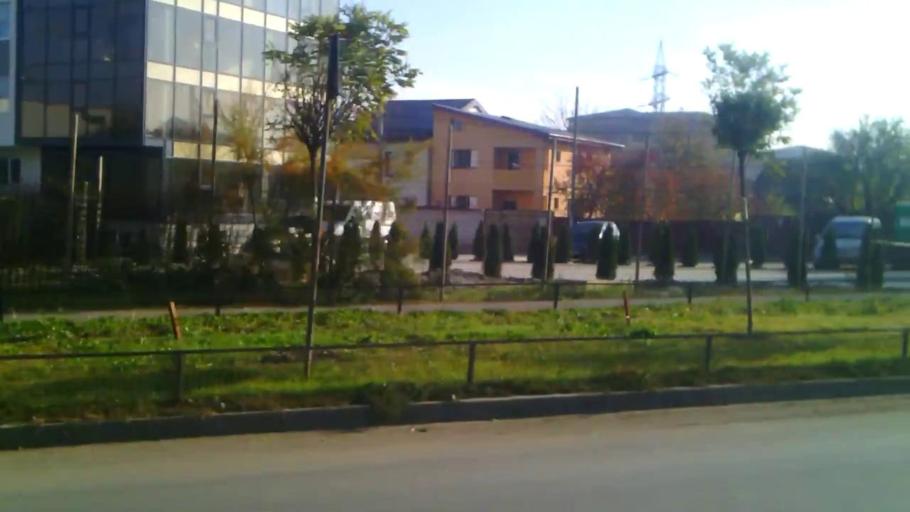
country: RO
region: Ilfov
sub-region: Comuna Popesti-Leordeni
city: Popesti-Leordeni
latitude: 44.3694
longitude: 26.1428
